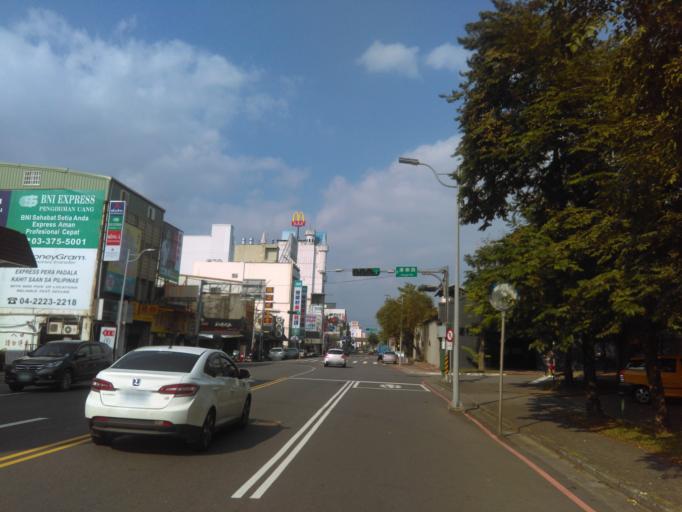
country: TW
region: Taiwan
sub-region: Yilan
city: Yilan
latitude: 24.7550
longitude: 121.7577
